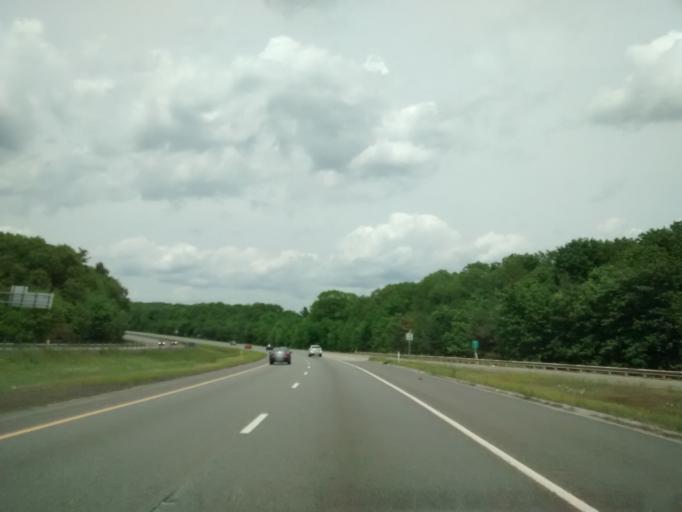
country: US
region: Massachusetts
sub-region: Worcester County
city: Whitinsville
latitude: 42.1293
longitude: -71.7025
